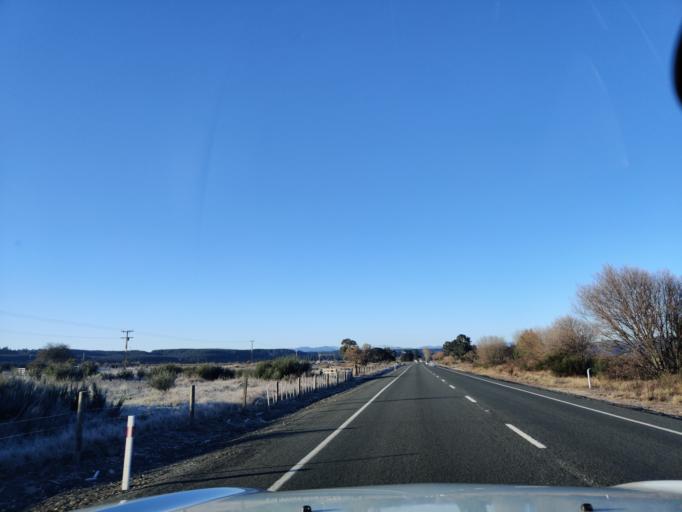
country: NZ
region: Waikato
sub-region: Taupo District
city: Taupo
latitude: -38.7666
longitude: 176.0760
